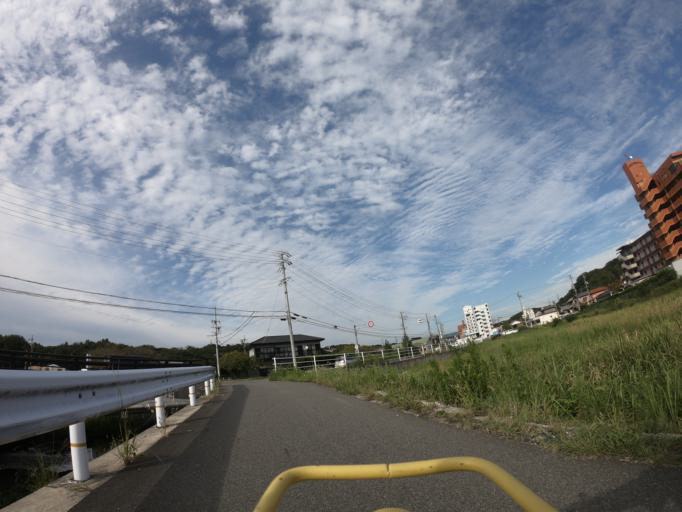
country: JP
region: Aichi
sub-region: Toyota-shi
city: Toyota
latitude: 35.1381
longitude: 137.0767
